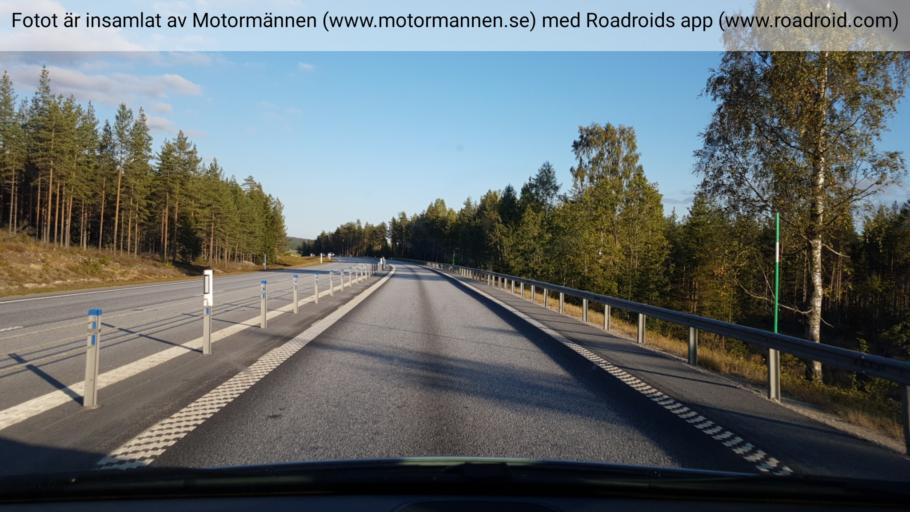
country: SE
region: Vaesterbotten
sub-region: Vannas Kommun
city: Vannasby
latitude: 63.8885
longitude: 20.0008
